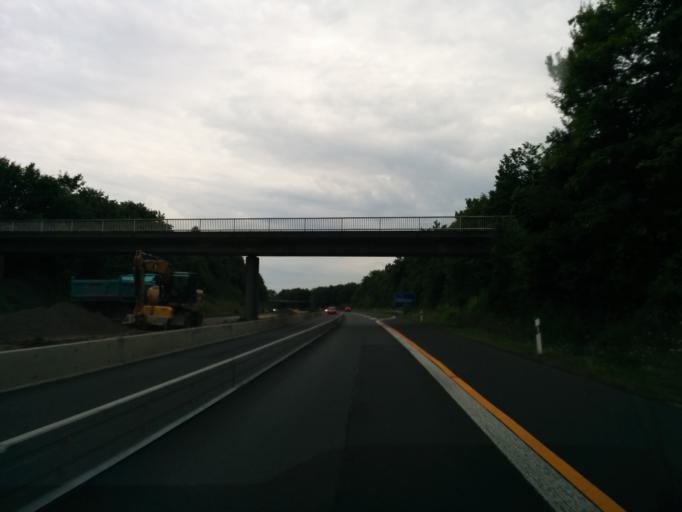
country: DE
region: Hesse
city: Fritzlar
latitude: 51.1517
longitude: 9.2966
